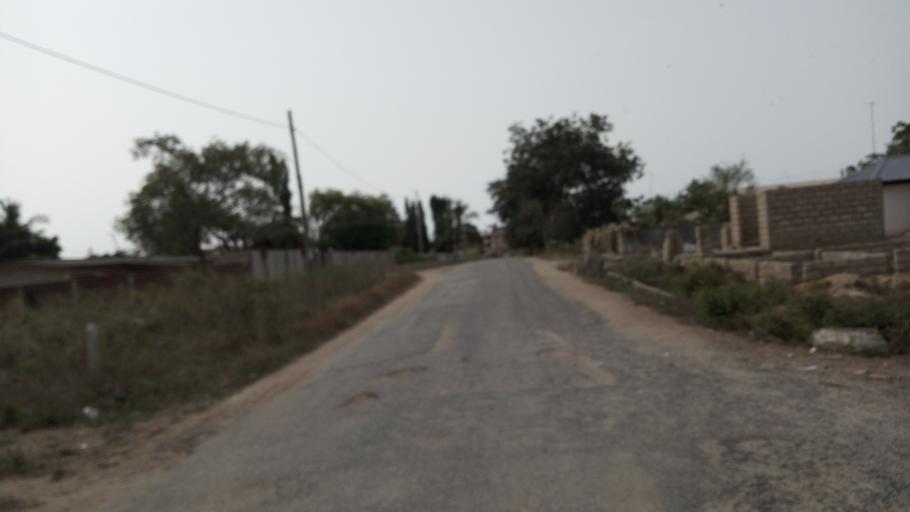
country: GH
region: Central
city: Winneba
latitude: 5.3698
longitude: -0.6412
